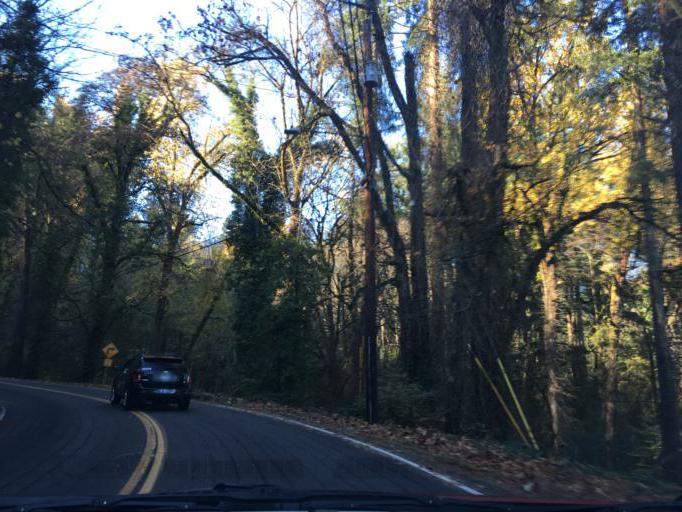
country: US
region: Oregon
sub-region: Washington County
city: Cedar Mill
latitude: 45.5896
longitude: -122.7810
